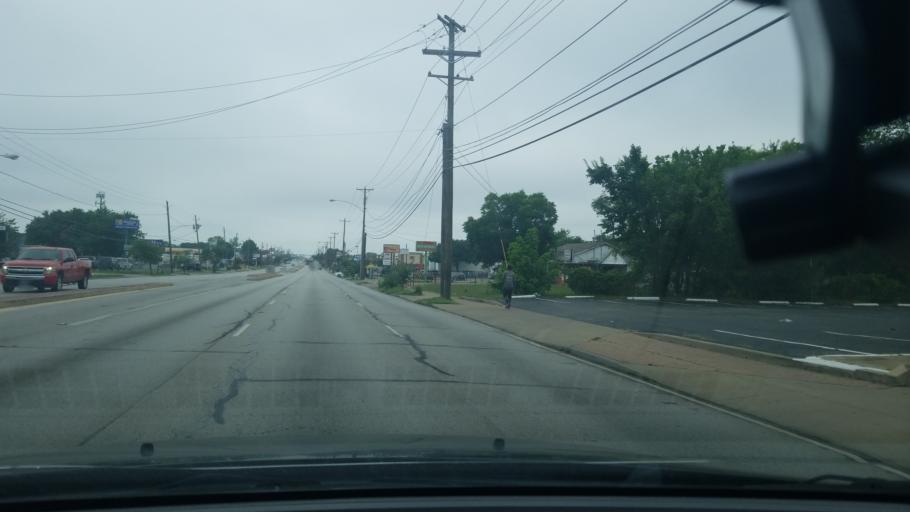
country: US
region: Texas
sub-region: Dallas County
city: Balch Springs
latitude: 32.7568
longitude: -96.6829
